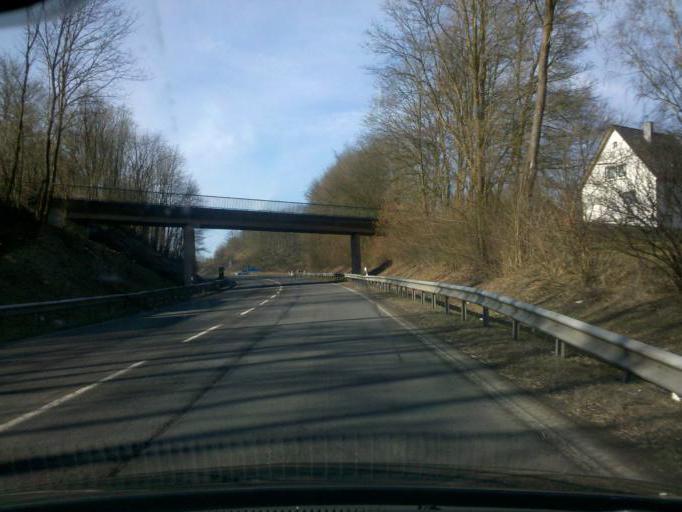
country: DE
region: North Rhine-Westphalia
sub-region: Regierungsbezirk Arnsberg
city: Drolshagen
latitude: 51.0556
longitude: 7.7627
